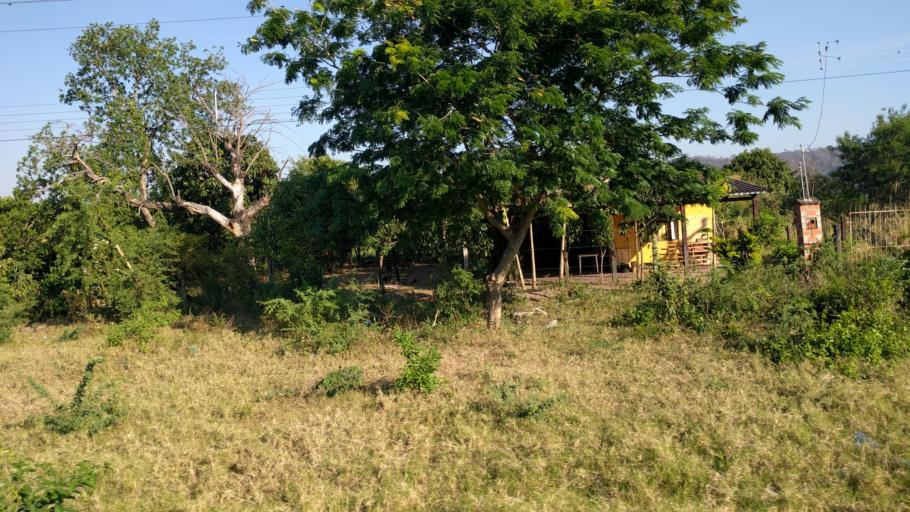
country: BO
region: Santa Cruz
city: Jorochito
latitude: -18.1485
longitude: -63.4870
